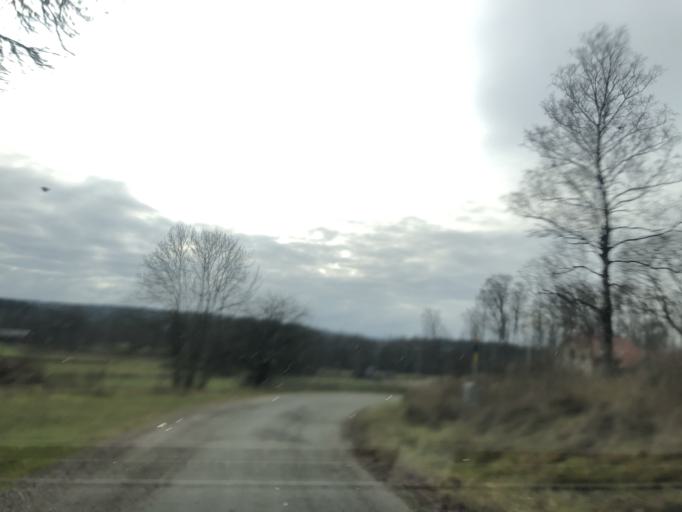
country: SE
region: Vaestra Goetaland
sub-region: Boras Kommun
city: Dalsjofors
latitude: 57.8311
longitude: 13.1735
